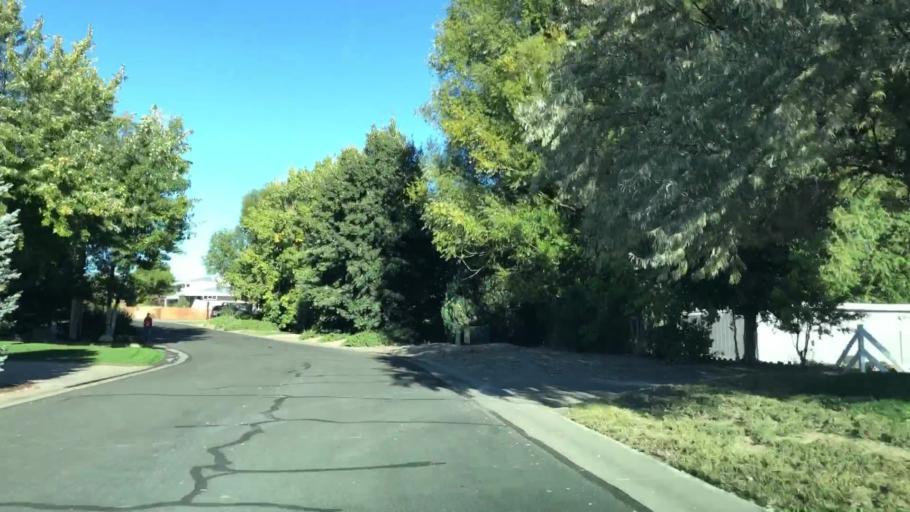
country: US
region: Colorado
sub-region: Larimer County
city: Campion
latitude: 40.3772
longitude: -105.1491
